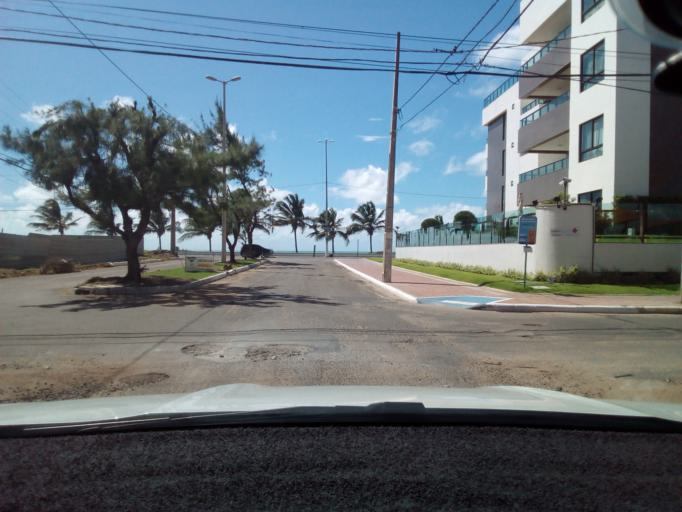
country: BR
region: Paraiba
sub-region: Joao Pessoa
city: Joao Pessoa
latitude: -7.0522
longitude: -34.8436
